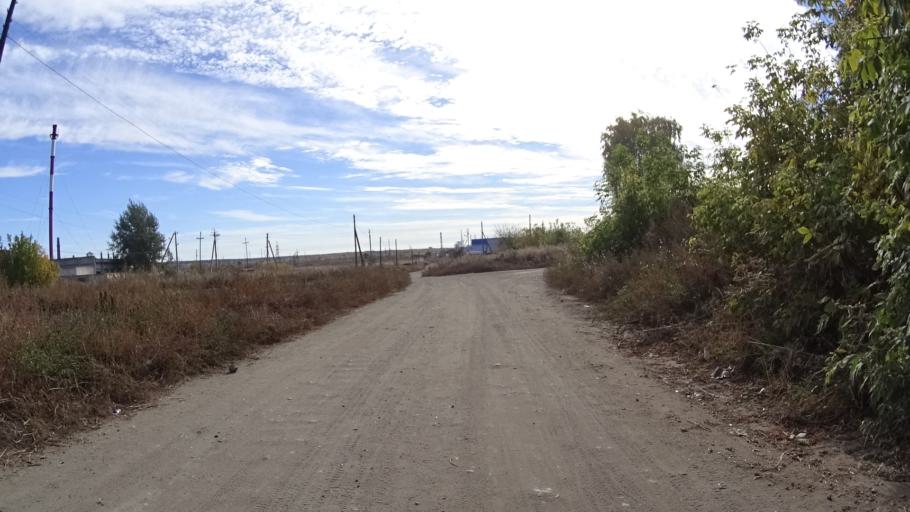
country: RU
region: Chelyabinsk
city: Troitsk
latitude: 54.0766
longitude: 61.5870
